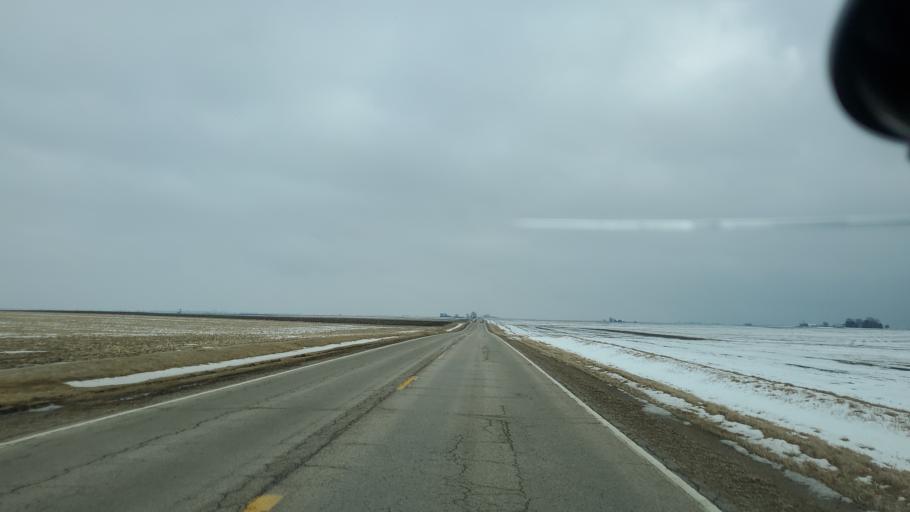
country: US
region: Illinois
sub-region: Marshall County
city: Wenona
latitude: 41.1188
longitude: -89.1369
